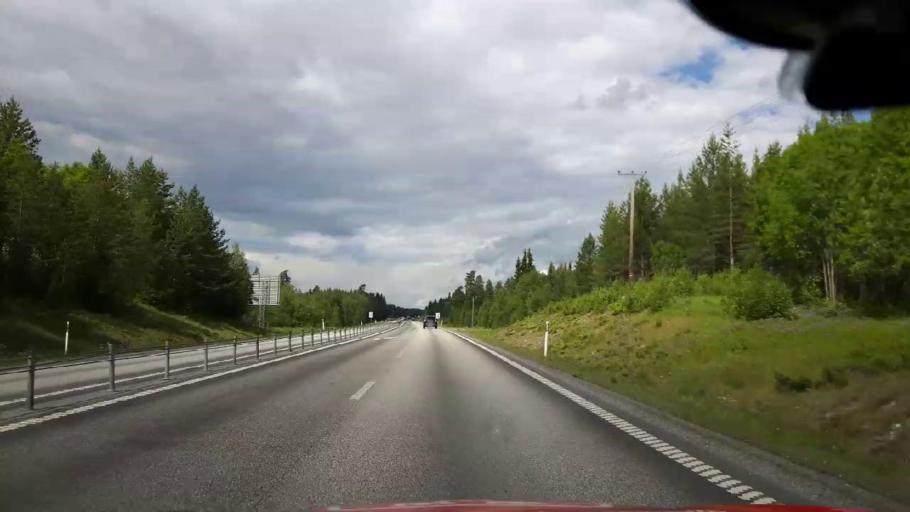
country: SE
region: Jaemtland
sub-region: OEstersunds Kommun
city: Ostersund
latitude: 63.2240
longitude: 14.6239
